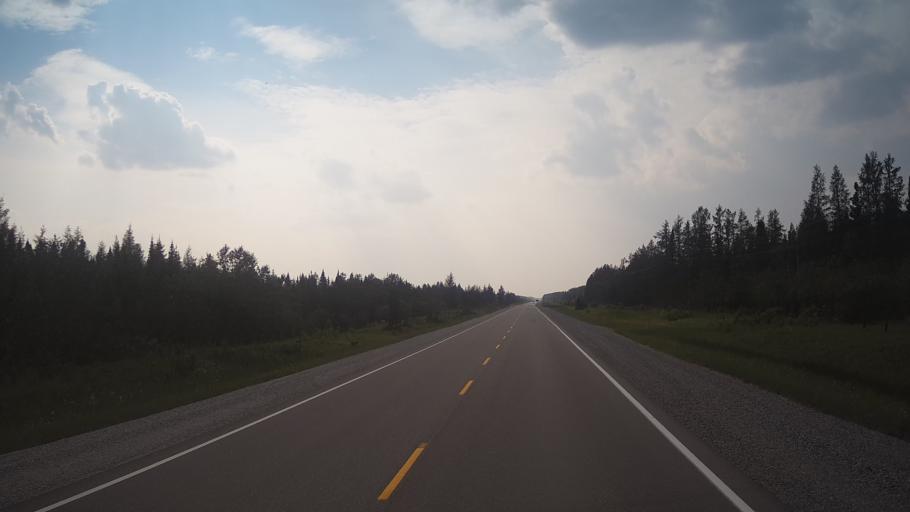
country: CA
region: Ontario
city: Kapuskasing
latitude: 49.5550
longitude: -83.0116
